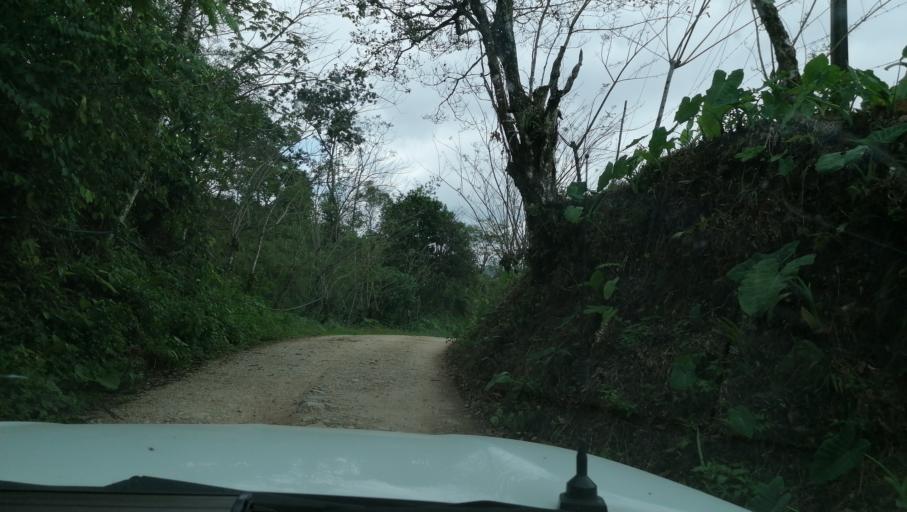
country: MX
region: Chiapas
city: Ocotepec
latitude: 17.2769
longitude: -93.2300
